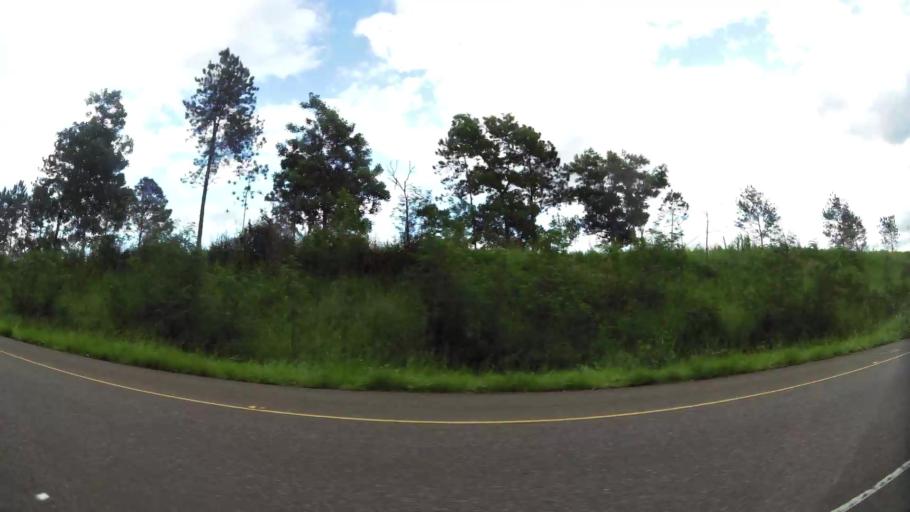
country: DO
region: Monsenor Nouel
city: Sabana del Puerto
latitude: 19.0942
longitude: -70.4380
